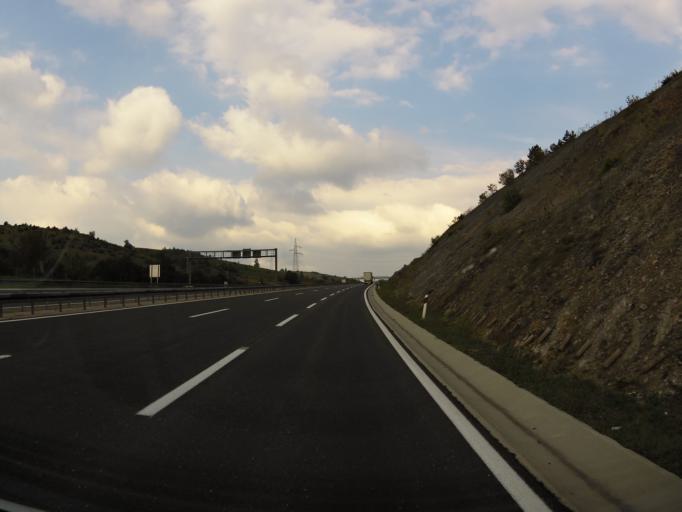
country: HR
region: Licko-Senjska
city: Brinje
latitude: 45.0126
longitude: 15.1376
